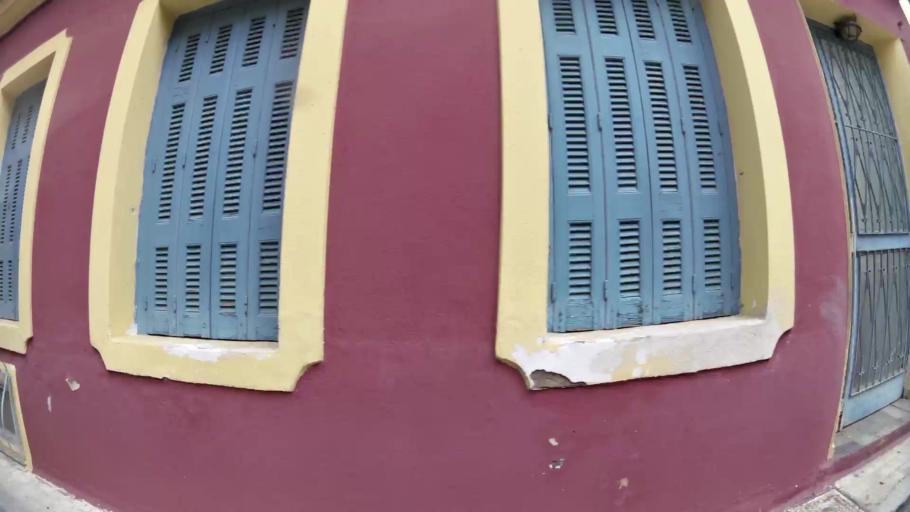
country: GR
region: Attica
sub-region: Nomos Attikis
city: Piraeus
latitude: 37.9422
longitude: 23.6562
